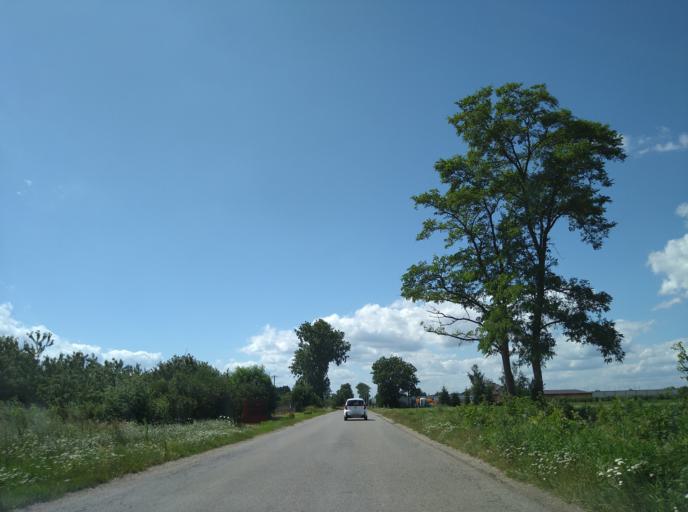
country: PL
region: Masovian Voivodeship
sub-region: Powiat bialobrzeski
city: Bialobrzegi
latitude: 51.6708
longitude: 20.8987
